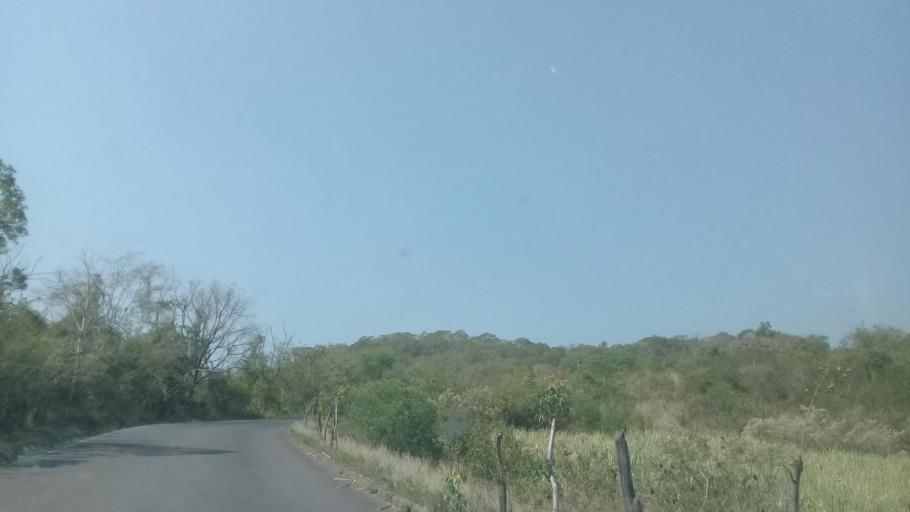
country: MX
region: Veracruz
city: El Castillo
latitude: 19.5779
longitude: -96.8298
